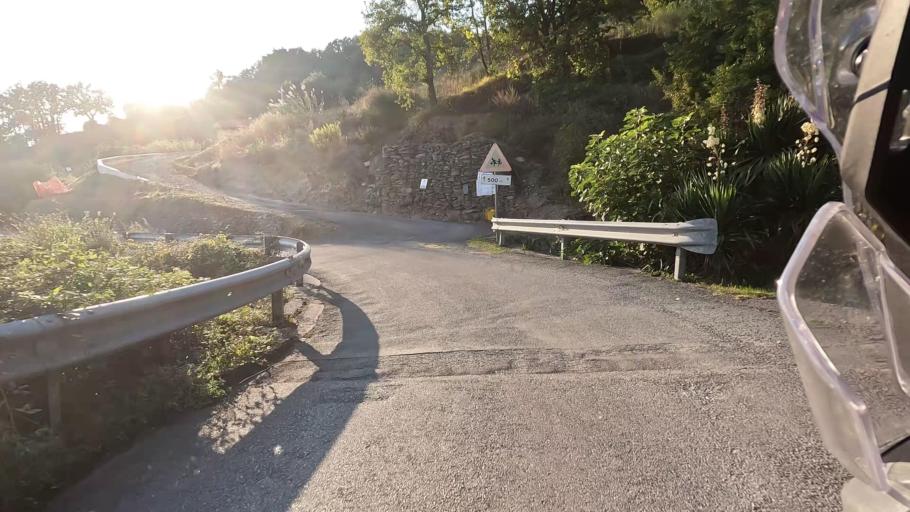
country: IT
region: Liguria
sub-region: Provincia di Savona
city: San Giovanni
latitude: 44.3930
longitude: 8.5186
